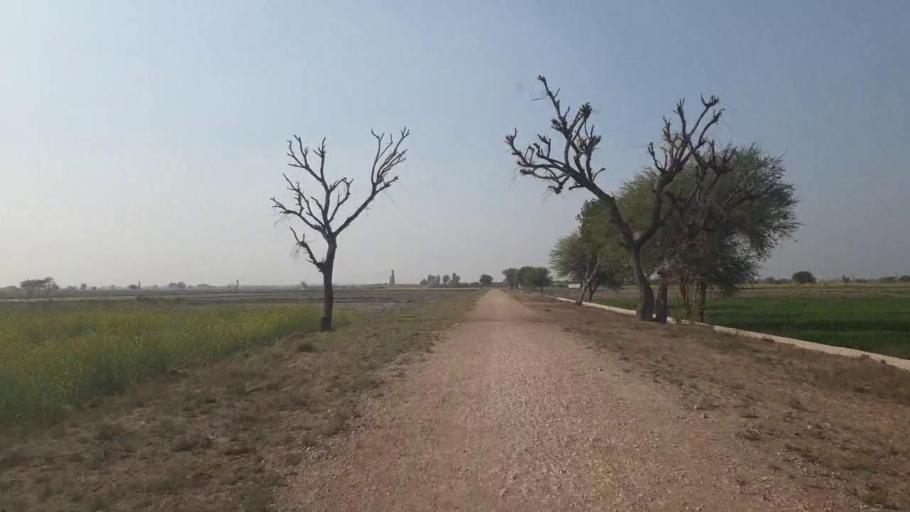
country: PK
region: Sindh
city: Tando Allahyar
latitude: 25.4394
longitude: 68.7056
